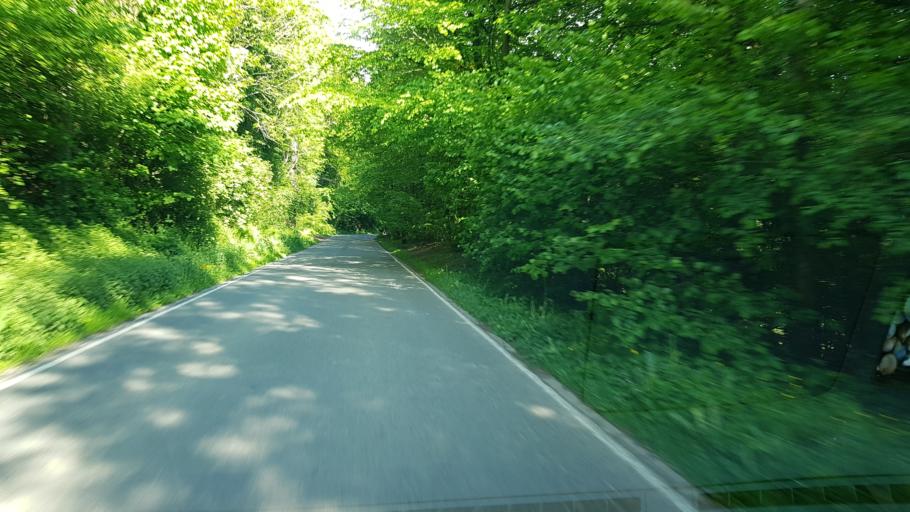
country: BE
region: Wallonia
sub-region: Province de Liege
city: Esneux
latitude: 50.5402
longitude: 5.6117
